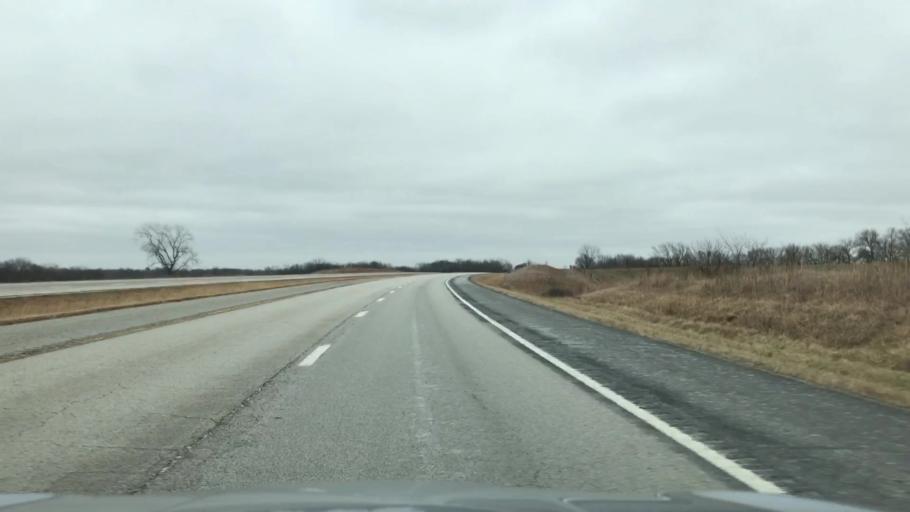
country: US
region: Missouri
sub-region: Caldwell County
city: Hamilton
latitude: 39.7482
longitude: -94.0523
